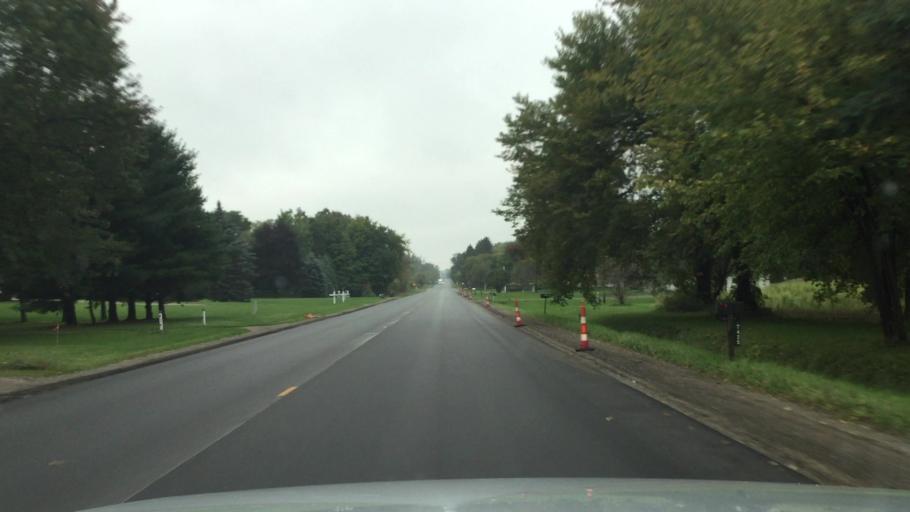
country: US
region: Michigan
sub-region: Shiawassee County
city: Perry
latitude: 42.8870
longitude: -84.2219
